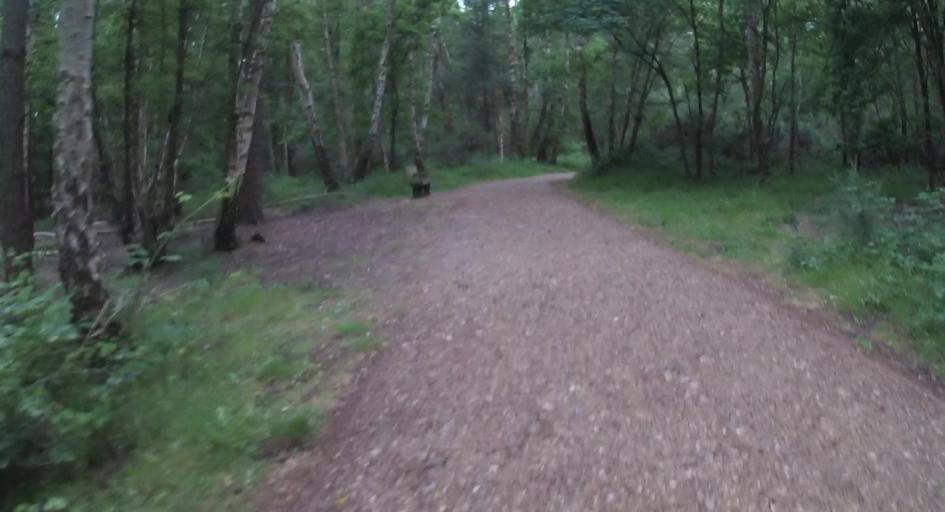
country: GB
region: England
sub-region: Hampshire
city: Farnborough
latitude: 51.2852
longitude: -0.7910
